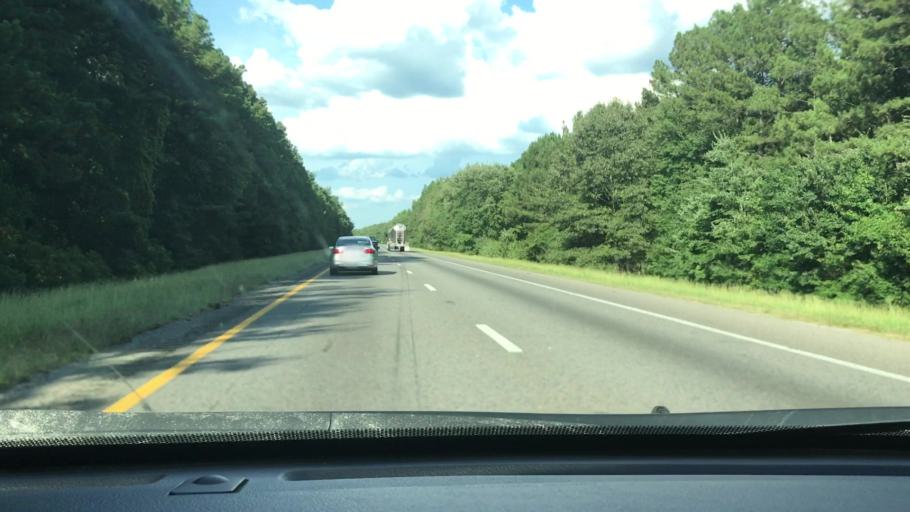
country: US
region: South Carolina
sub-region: Dillon County
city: Latta
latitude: 34.3178
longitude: -79.5929
